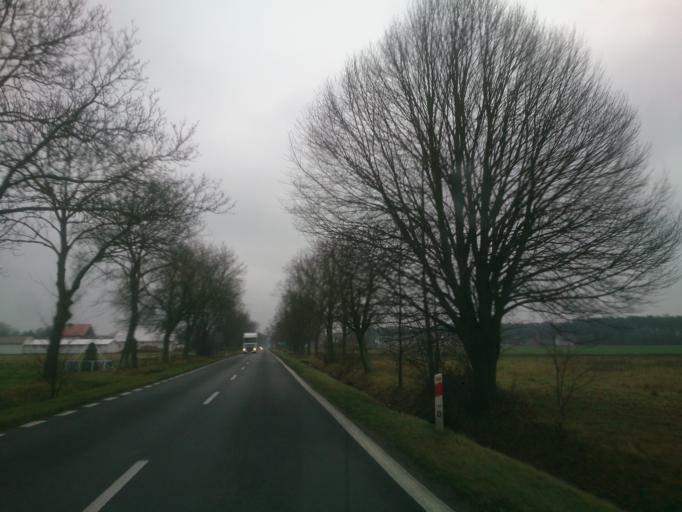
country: PL
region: Masovian Voivodeship
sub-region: Powiat sierpecki
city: Szczutowo
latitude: 52.9157
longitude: 19.6257
